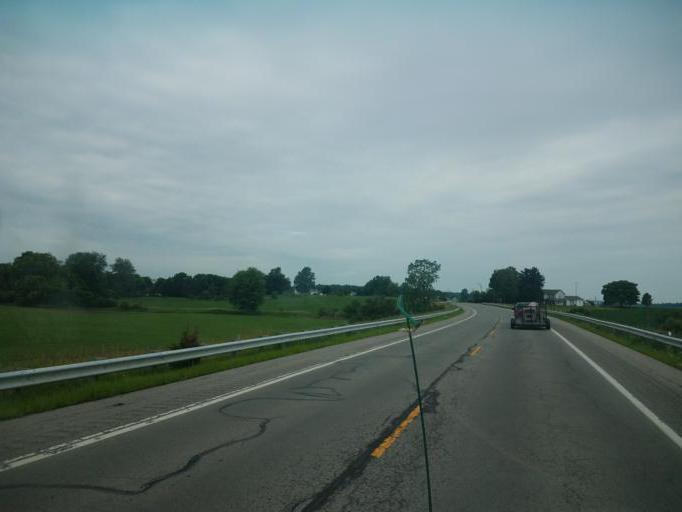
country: US
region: Ohio
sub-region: Hardin County
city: Ada
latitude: 40.7166
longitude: -83.7636
